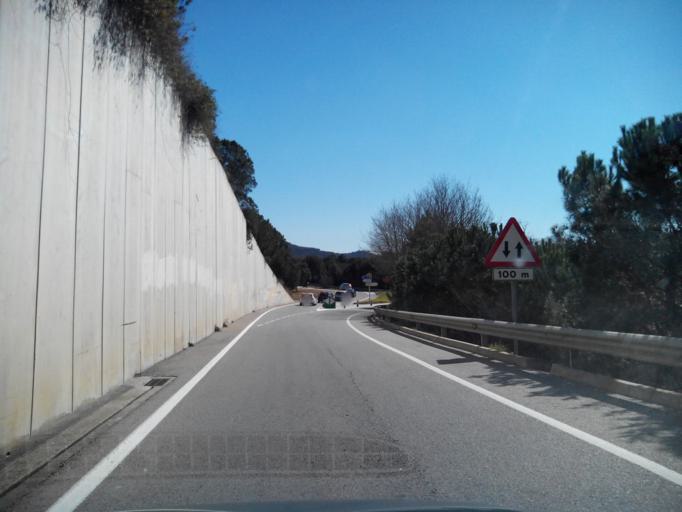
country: ES
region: Catalonia
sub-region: Provincia de Barcelona
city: Argentona
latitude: 41.5733
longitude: 2.3871
